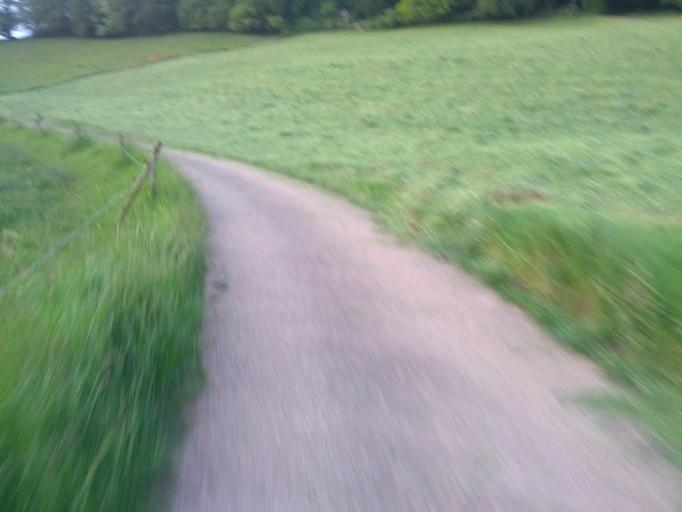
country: DE
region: Baden-Wuerttemberg
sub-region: Freiburg Region
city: Wittnau
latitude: 47.9531
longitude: 7.8026
